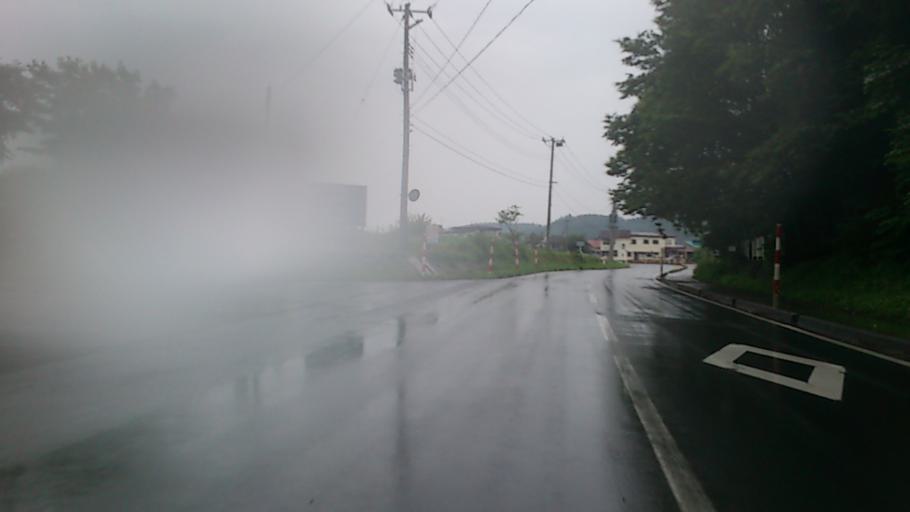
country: JP
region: Akita
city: Takanosu
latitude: 40.2659
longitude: 140.2577
